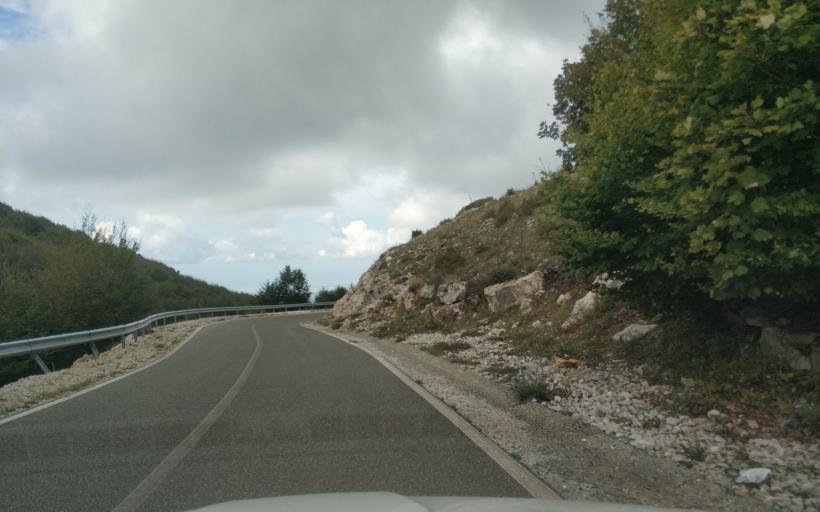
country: AL
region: Durres
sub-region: Rrethi i Krujes
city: Kruje
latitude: 41.5192
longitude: 19.8072
